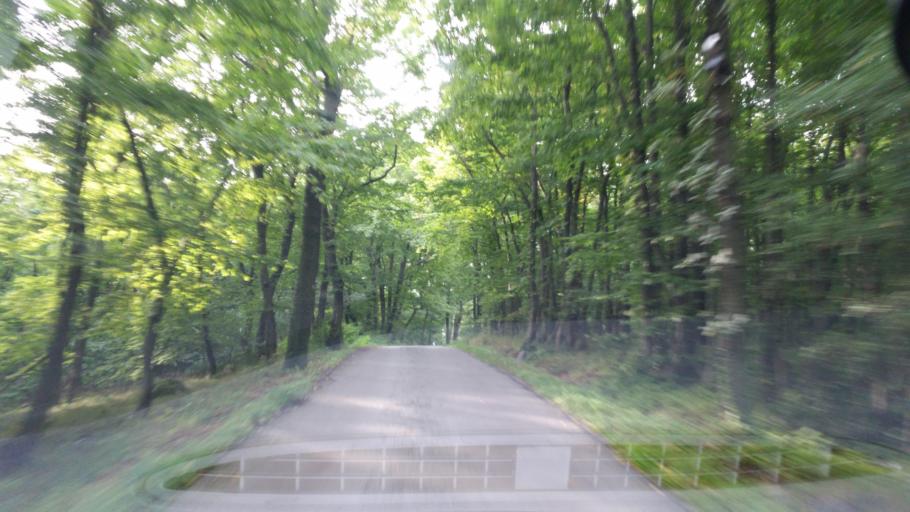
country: DE
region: Saxony
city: Sohland am Rotstein
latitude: 51.1106
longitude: 14.7605
